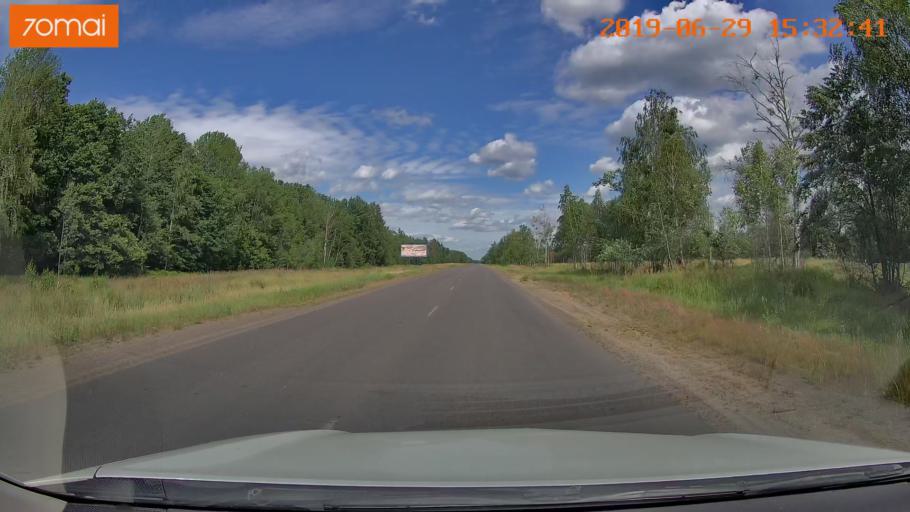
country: BY
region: Brest
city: Mikashevichy
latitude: 52.2103
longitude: 27.4227
